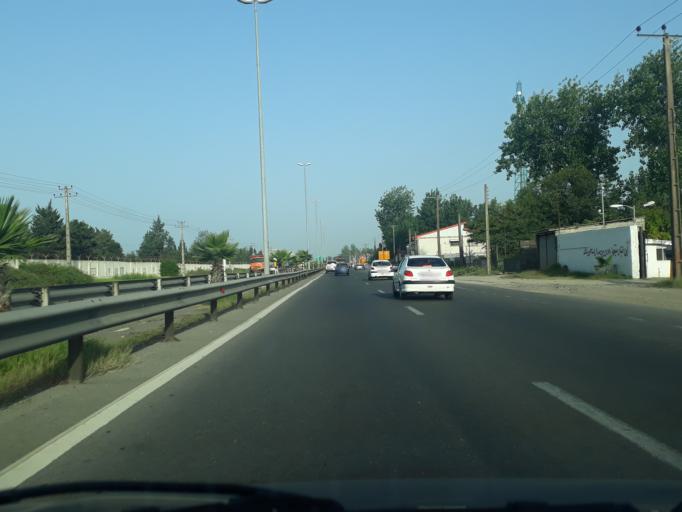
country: IR
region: Gilan
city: Bandar-e Anzali
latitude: 37.4581
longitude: 49.6045
